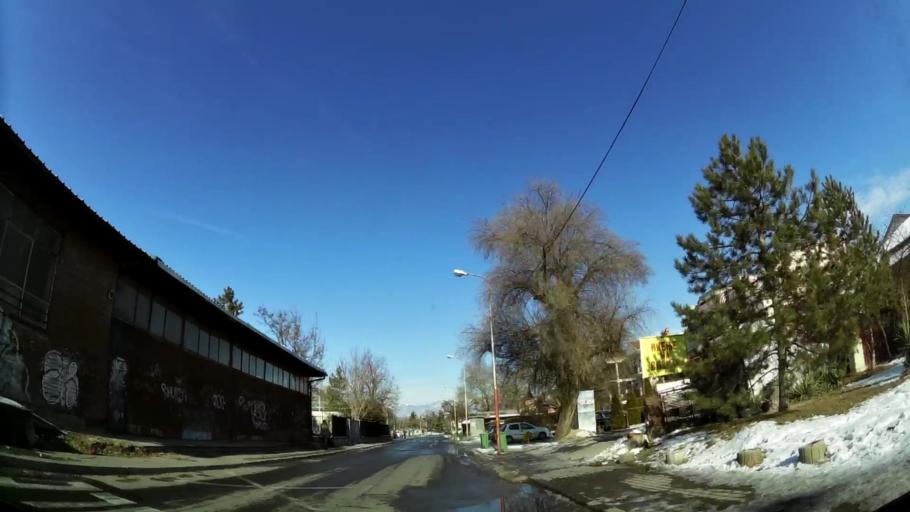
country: MK
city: Krushopek
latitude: 42.0056
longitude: 21.3748
